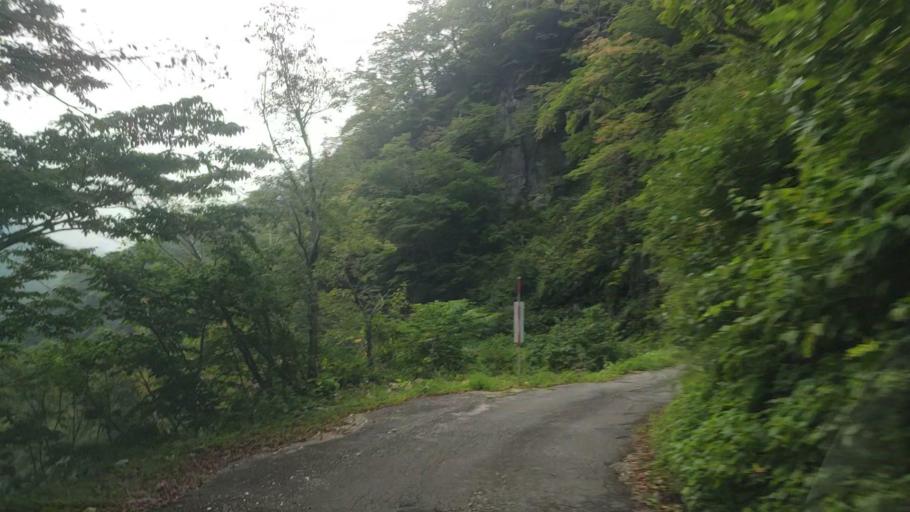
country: JP
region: Toyama
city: Yatsuomachi-higashikumisaka
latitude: 36.3934
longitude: 137.0787
